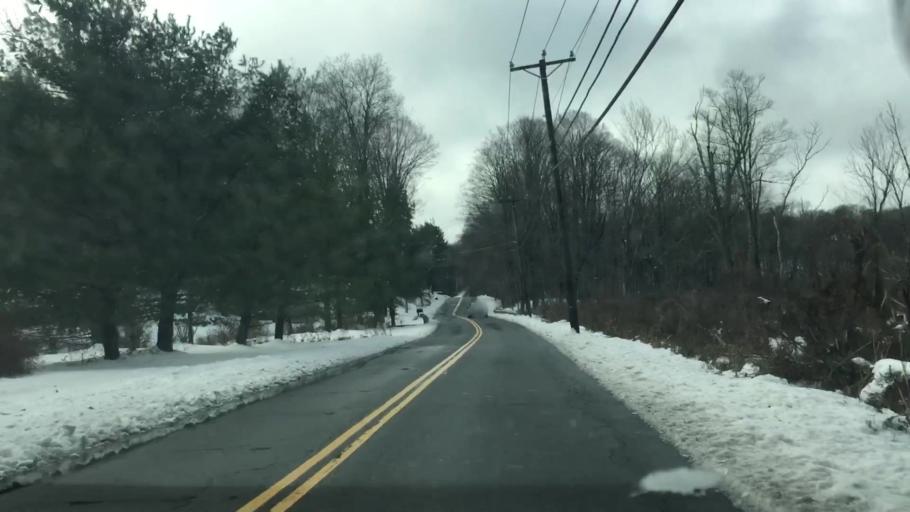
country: US
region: Connecticut
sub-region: Fairfield County
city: Danbury
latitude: 41.3635
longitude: -73.5049
